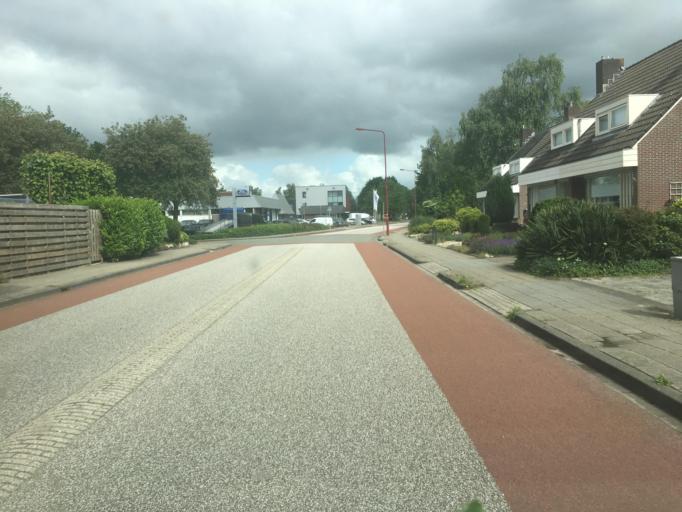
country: NL
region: Friesland
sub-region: Gemeente Heerenveen
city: Heerenveen
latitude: 52.9503
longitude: 5.9143
